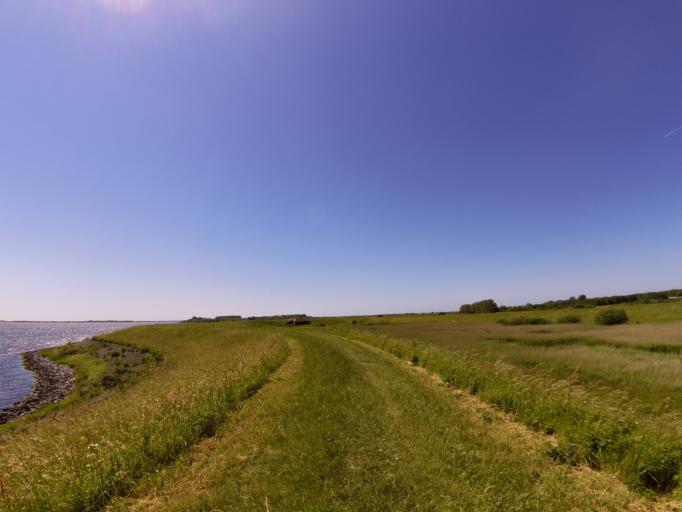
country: NL
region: South Holland
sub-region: Gemeente Goeree-Overflakkee
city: Ouddorp
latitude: 51.7935
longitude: 3.9102
